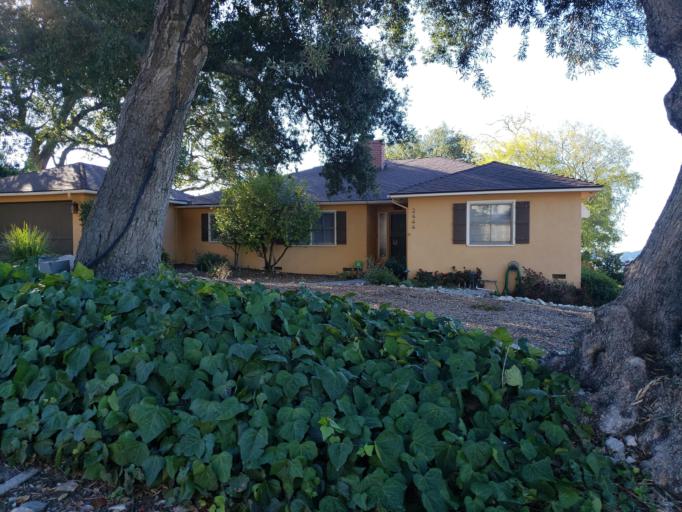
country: US
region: California
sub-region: Los Angeles County
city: La Crescenta-Montrose
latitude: 34.2366
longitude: -118.2327
